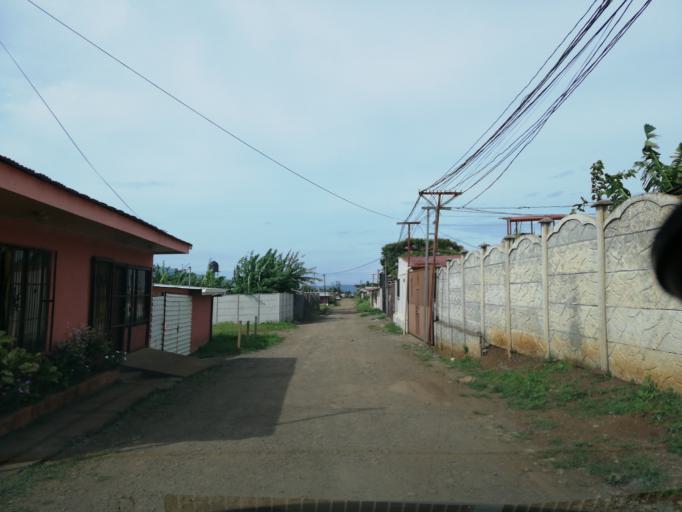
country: CR
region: Alajuela
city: Alajuela
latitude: 10.0134
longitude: -84.1931
